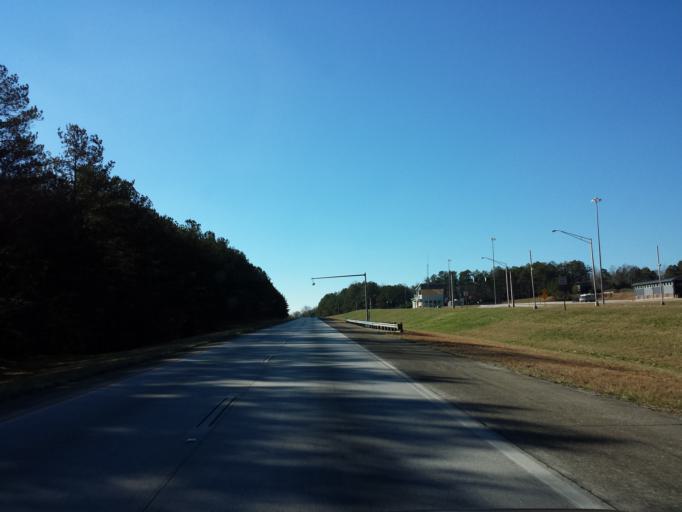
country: US
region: Georgia
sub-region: Carroll County
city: Temple
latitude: 33.6965
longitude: -85.0828
